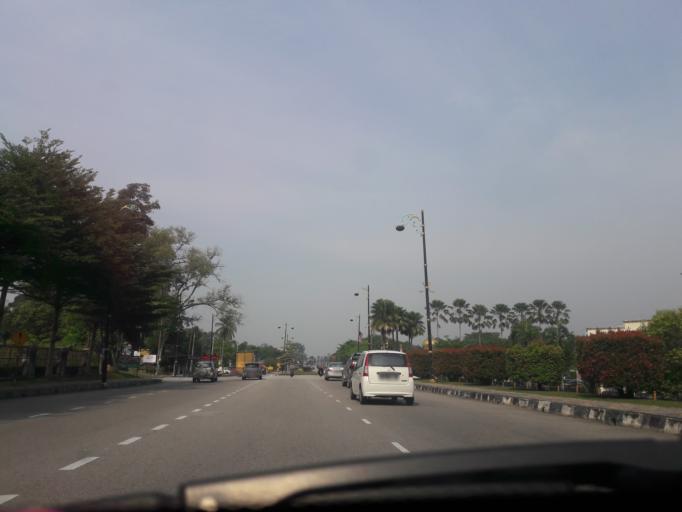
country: MY
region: Kedah
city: Kulim
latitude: 5.3654
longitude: 100.5524
